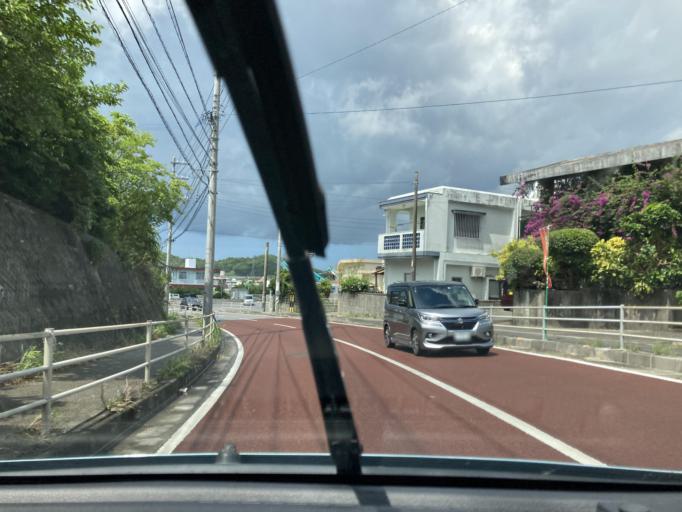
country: JP
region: Okinawa
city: Tomigusuku
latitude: 26.1807
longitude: 127.7424
